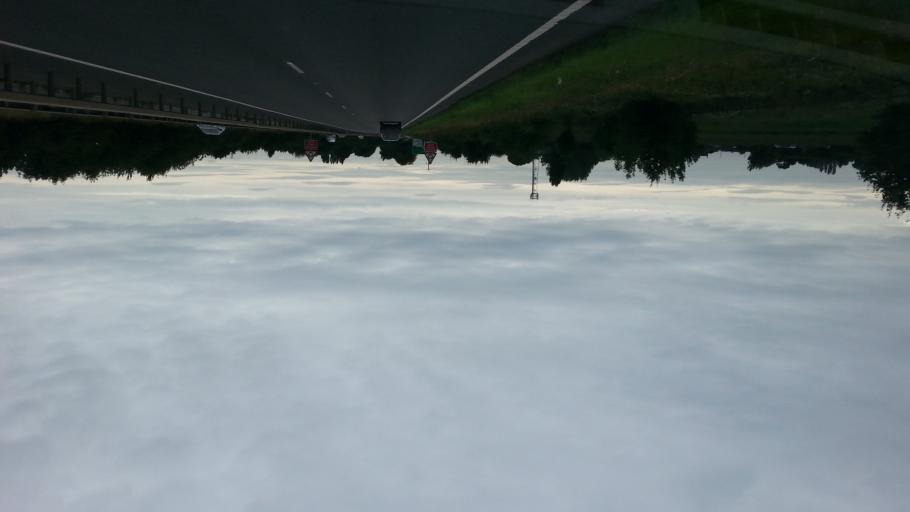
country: GB
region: England
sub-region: Peterborough
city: Thorney
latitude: 52.6264
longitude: -0.1002
